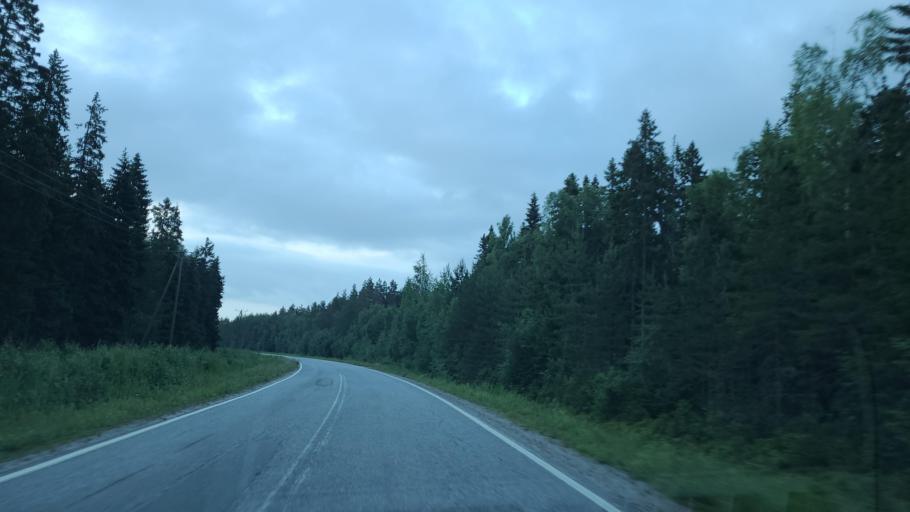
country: FI
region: Ostrobothnia
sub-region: Vaasa
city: Replot
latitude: 63.2103
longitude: 21.2541
